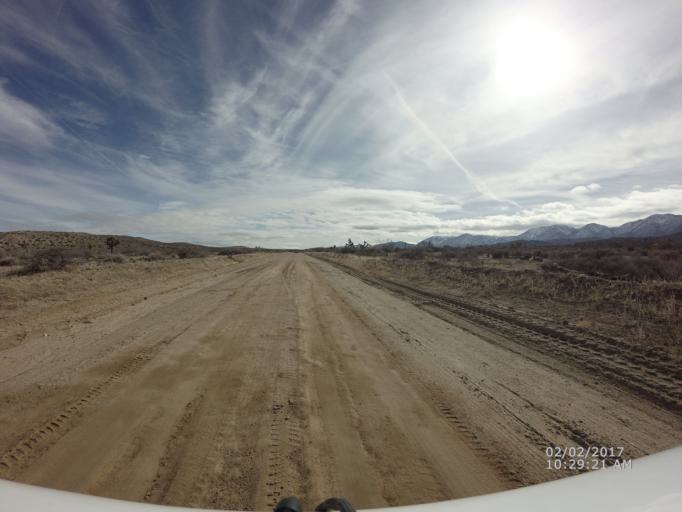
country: US
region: California
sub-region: Los Angeles County
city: Littlerock
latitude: 34.4863
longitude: -117.9326
